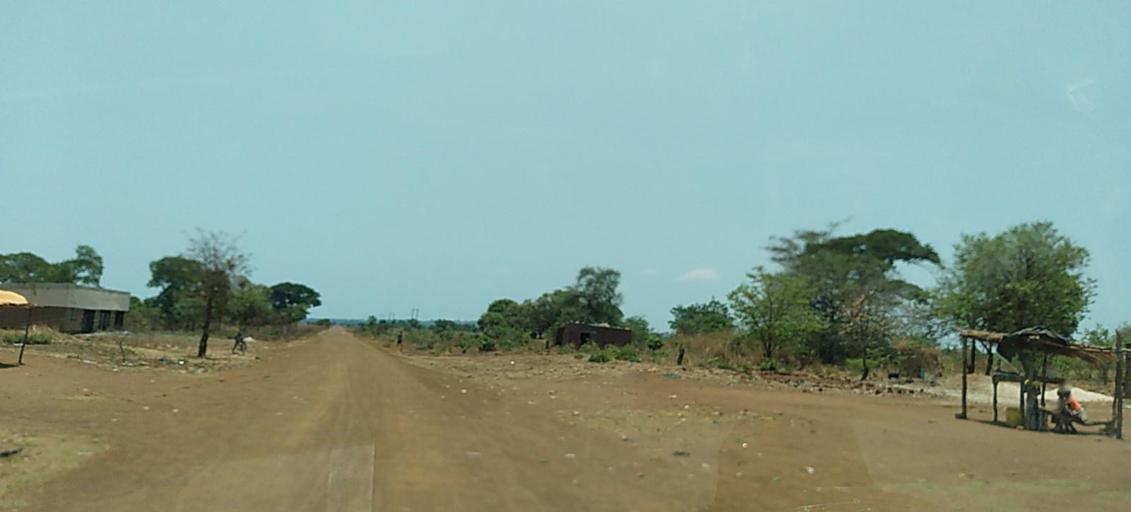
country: ZM
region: Copperbelt
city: Mpongwe
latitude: -13.6732
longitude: 27.8554
